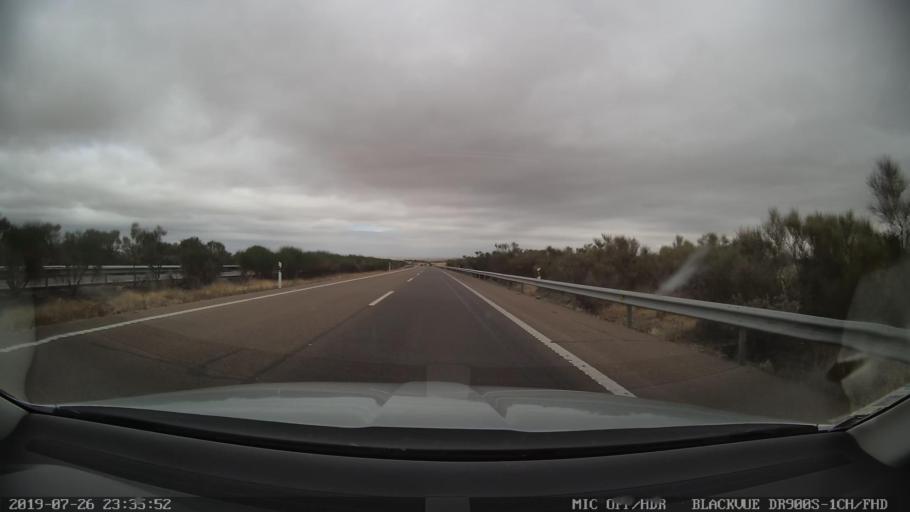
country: ES
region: Extremadura
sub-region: Provincia de Caceres
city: Santa Cruz de la Sierra
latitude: 39.3835
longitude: -5.8827
